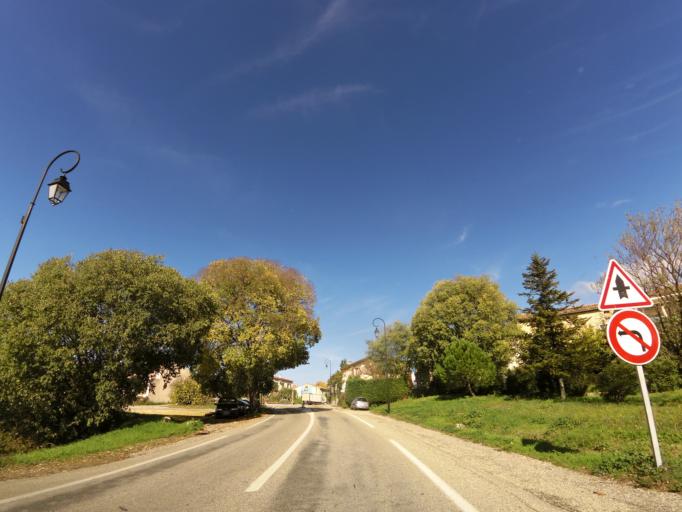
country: FR
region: Languedoc-Roussillon
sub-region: Departement du Gard
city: Ledignan
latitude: 43.9859
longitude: 4.1062
